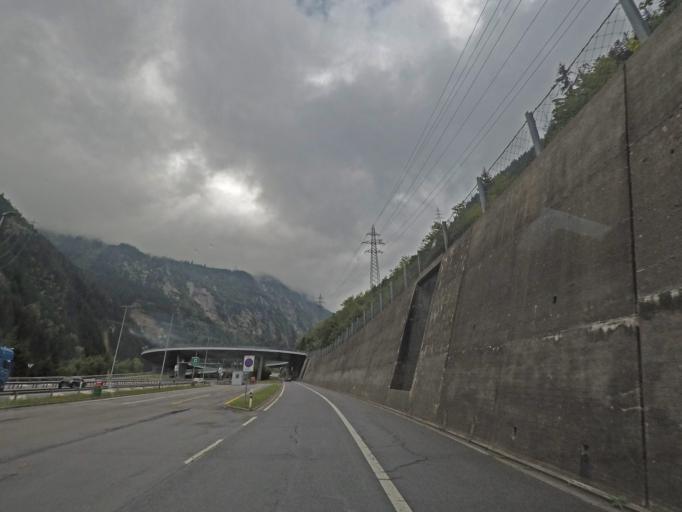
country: CH
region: Uri
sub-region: Uri
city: Andermatt
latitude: 46.6775
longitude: 8.5922
